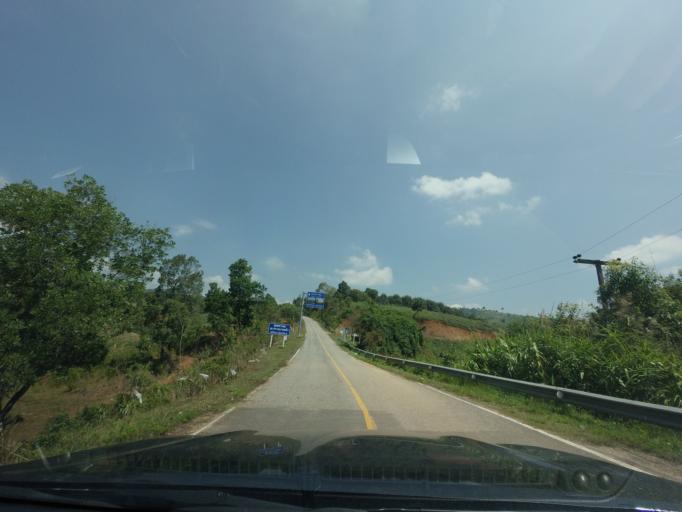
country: TH
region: Loei
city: Na Haeo
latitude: 17.5863
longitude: 100.9070
